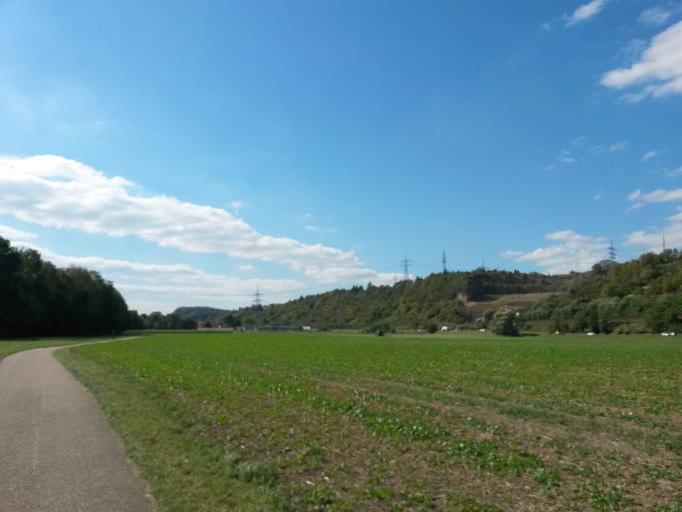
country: DE
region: Baden-Wuerttemberg
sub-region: Karlsruhe Region
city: Muhlacker
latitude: 48.9459
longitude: 8.8230
